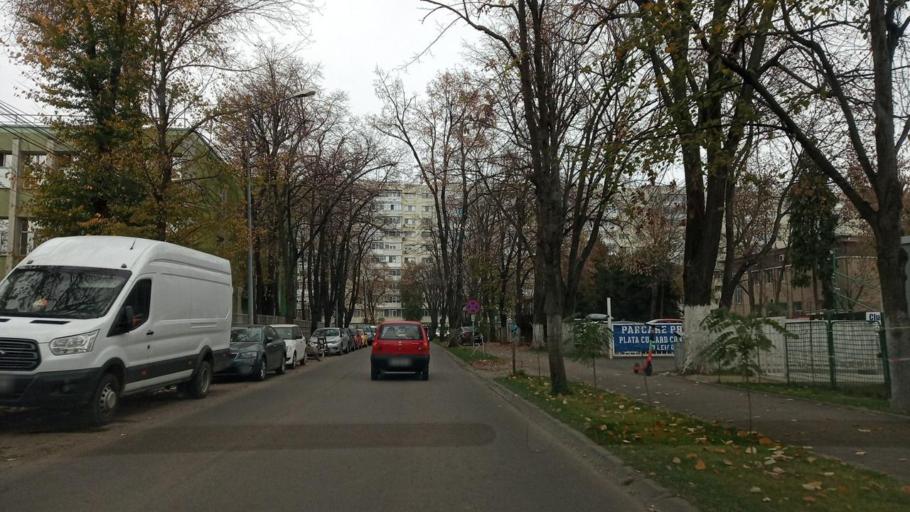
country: RO
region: Ilfov
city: Dobroesti
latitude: 44.4378
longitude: 26.1796
